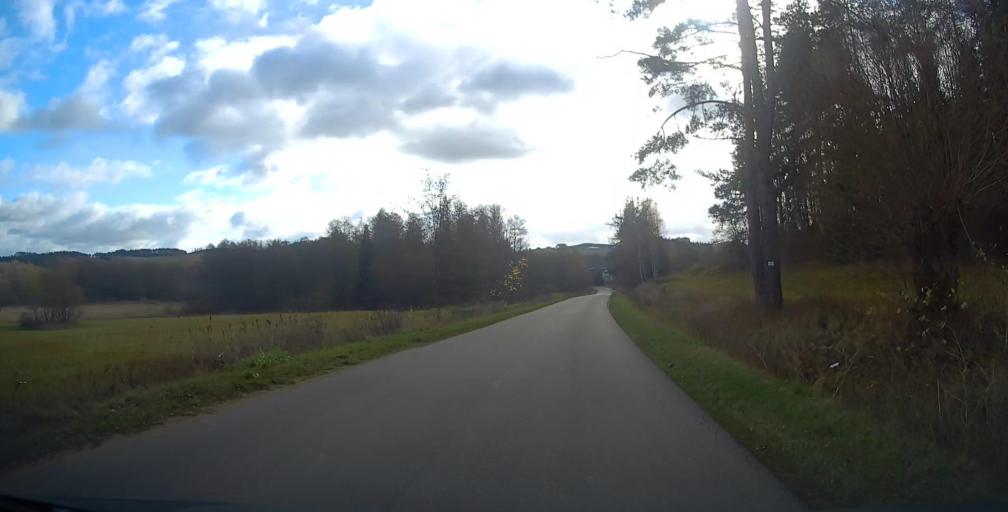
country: PL
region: Podlasie
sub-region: Suwalki
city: Suwalki
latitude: 54.2733
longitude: 22.9088
